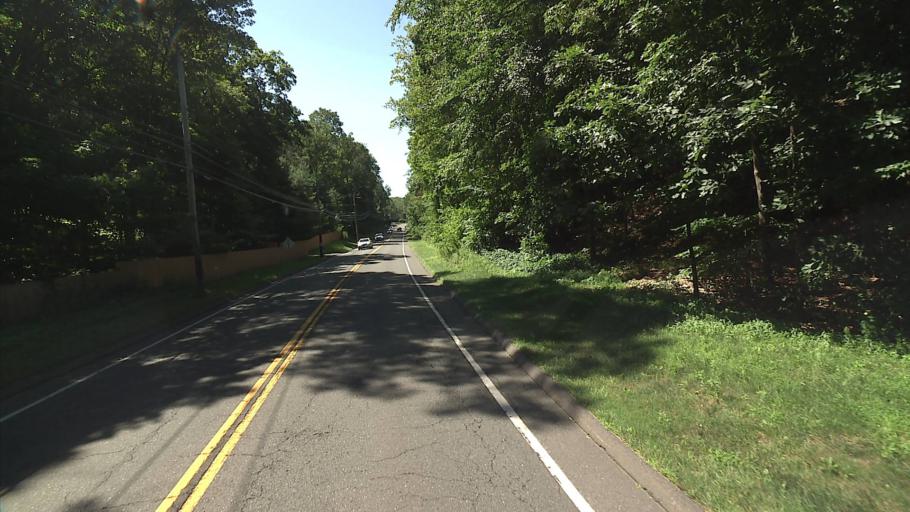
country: US
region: Connecticut
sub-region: Hartford County
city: Weatogue
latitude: 41.7825
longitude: -72.8180
